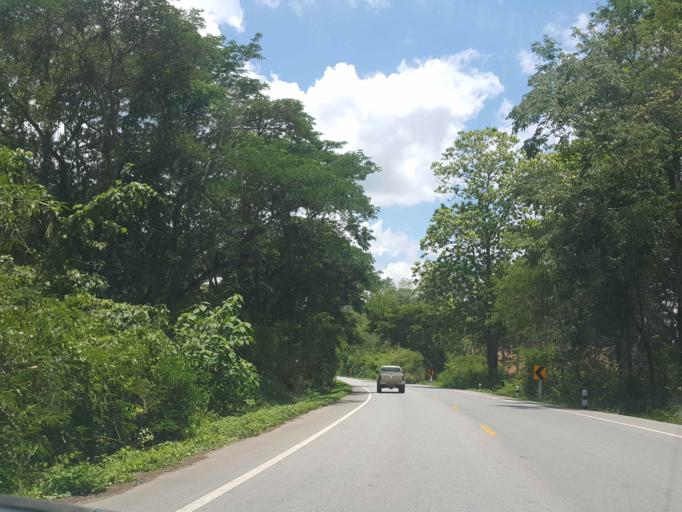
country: TH
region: Nan
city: Wiang Sa
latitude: 18.5236
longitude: 100.6115
